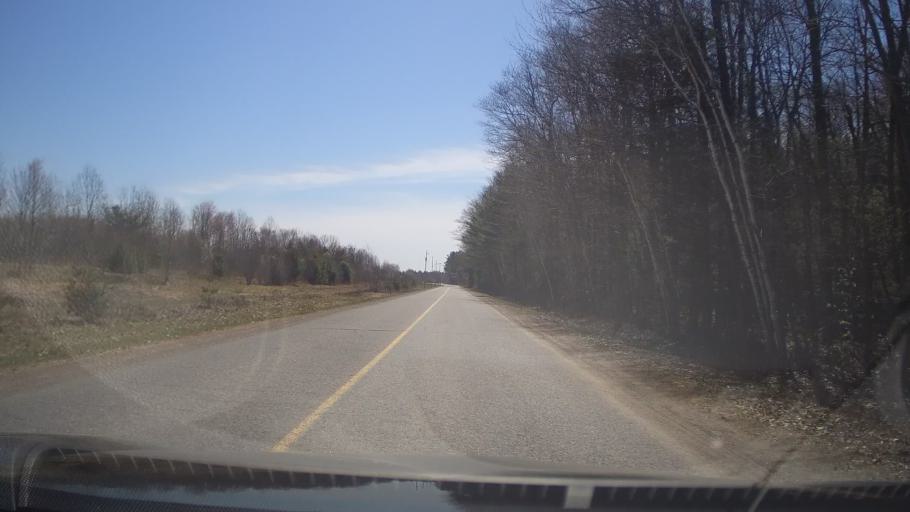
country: CA
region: Quebec
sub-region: Outaouais
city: Shawville
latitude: 45.5203
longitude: -76.4123
